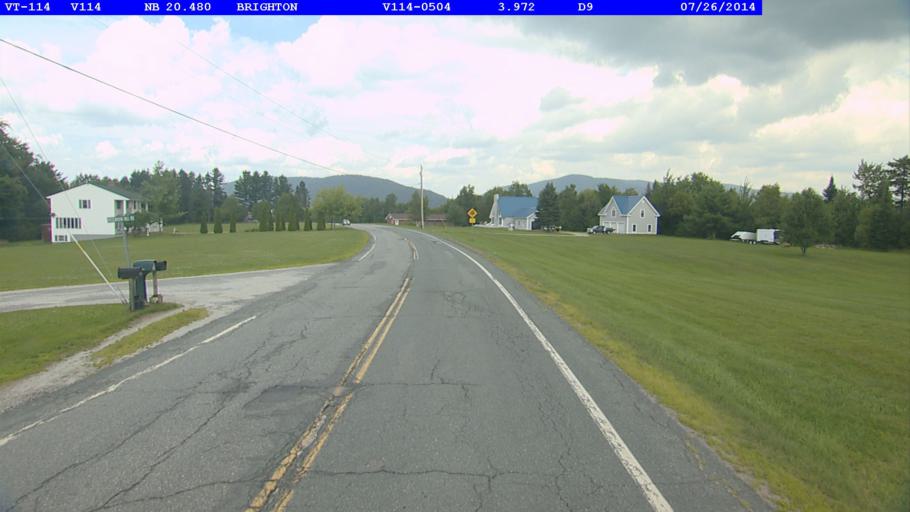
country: US
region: Vermont
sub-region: Caledonia County
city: Lyndonville
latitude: 44.7906
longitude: -71.9090
